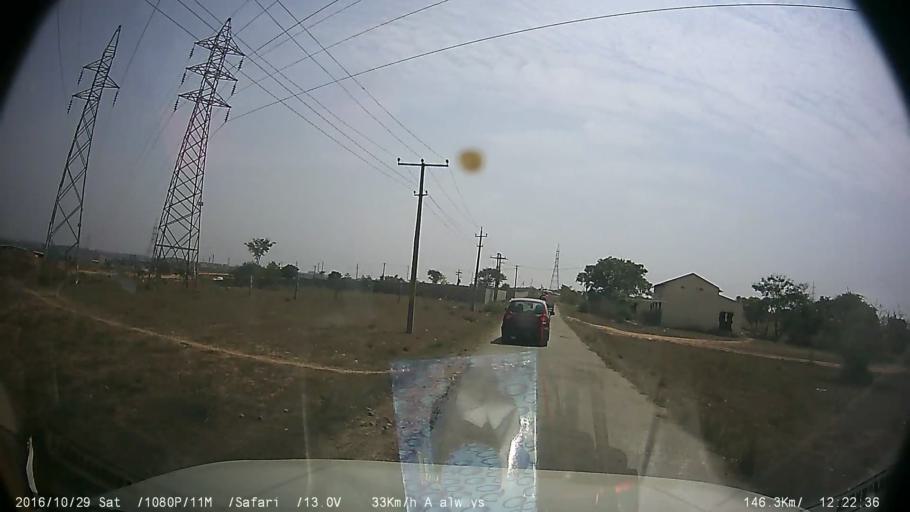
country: IN
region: Karnataka
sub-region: Mysore
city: Mysore
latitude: 12.3627
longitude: 76.5608
